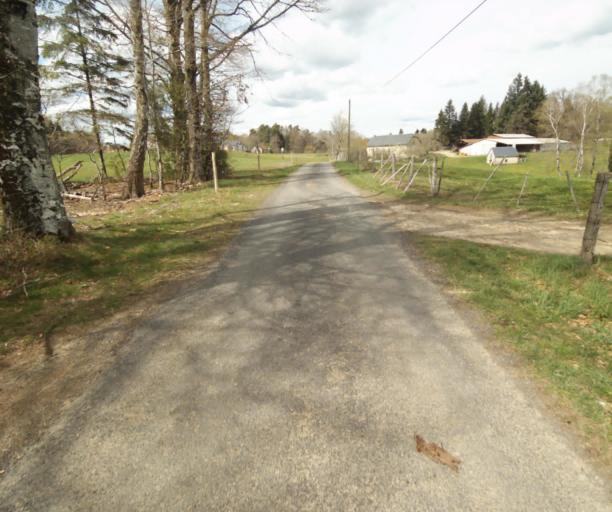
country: FR
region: Limousin
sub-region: Departement de la Correze
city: Argentat
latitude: 45.2015
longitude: 1.8939
